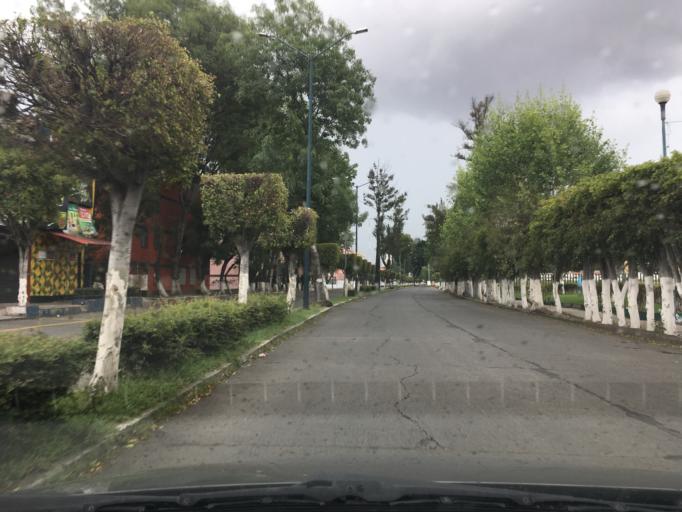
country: MX
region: Michoacan
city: Morelia
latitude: 19.7046
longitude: -101.2033
